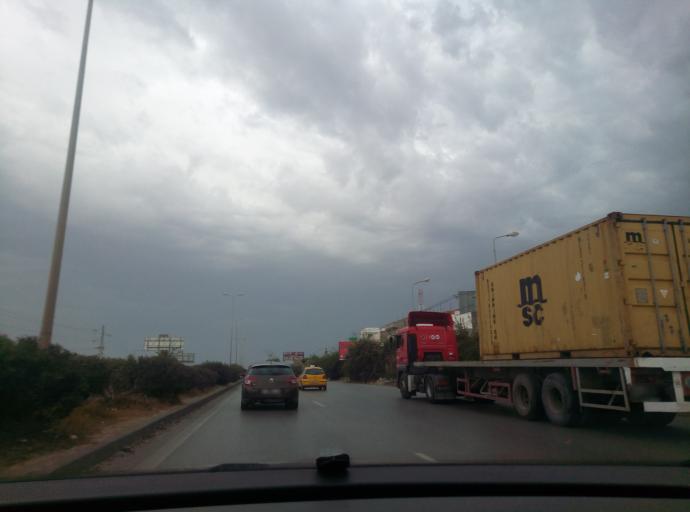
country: TN
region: Bin 'Arus
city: Ben Arous
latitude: 36.7518
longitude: 10.2048
